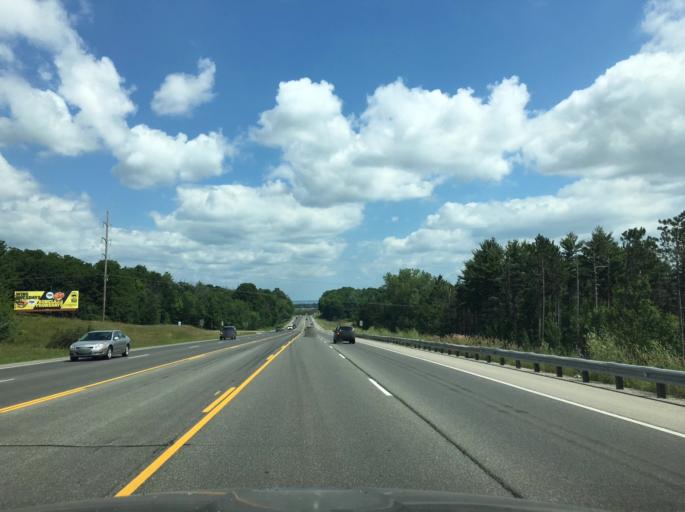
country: US
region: Michigan
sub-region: Grand Traverse County
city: Traverse City
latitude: 44.7063
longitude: -85.6529
